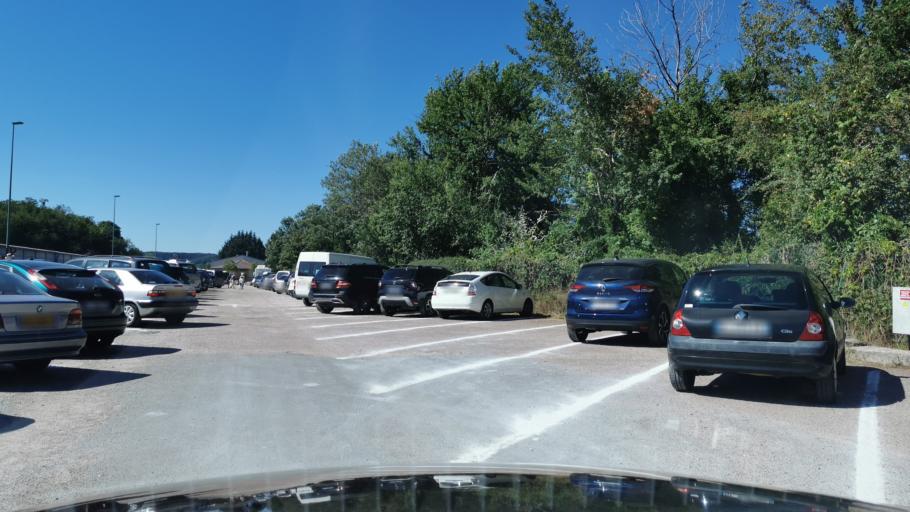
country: FR
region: Bourgogne
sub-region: Departement de Saone-et-Loire
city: Le Creusot
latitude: 46.8127
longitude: 4.4135
